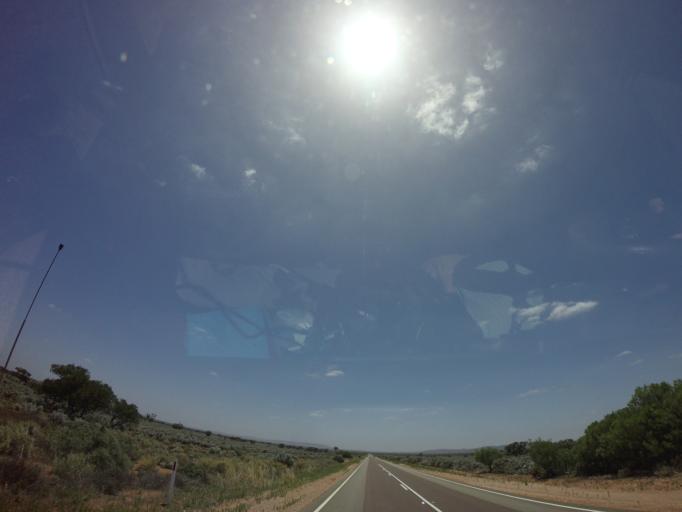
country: AU
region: South Australia
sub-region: Whyalla
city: Whyalla
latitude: -32.8162
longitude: 137.0455
